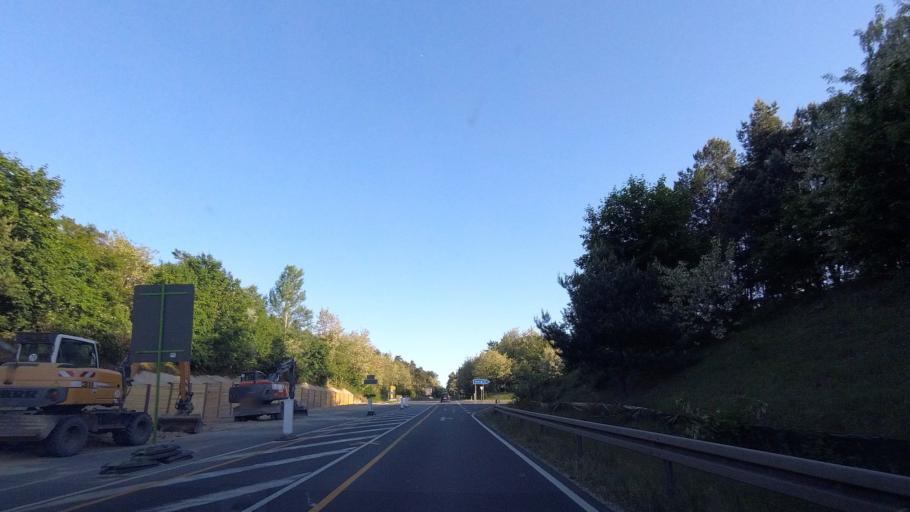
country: DE
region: Brandenburg
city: Brandenburg an der Havel
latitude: 52.3503
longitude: 12.5992
